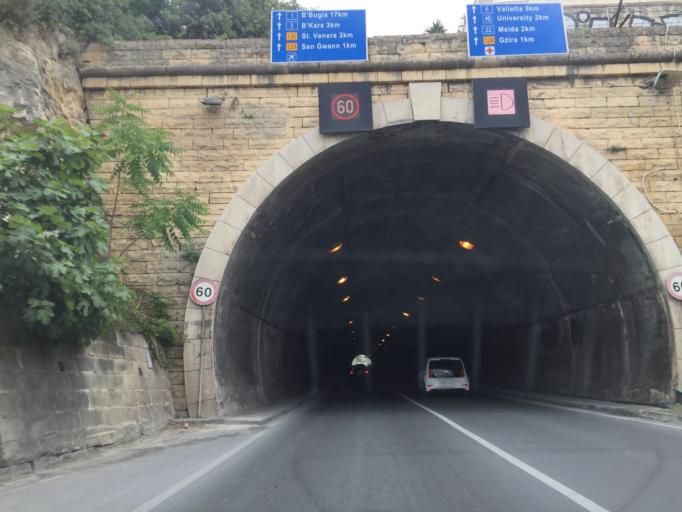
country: MT
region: Saint Julian
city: San Giljan
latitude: 35.9150
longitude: 14.4863
